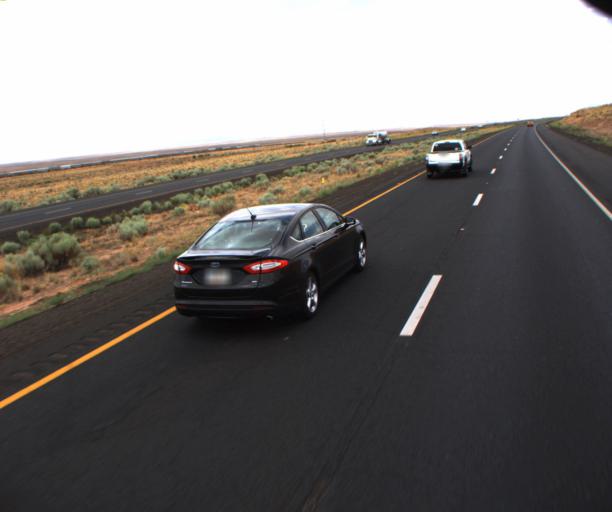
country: US
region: Arizona
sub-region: Navajo County
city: Joseph City
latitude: 34.9732
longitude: -110.5093
